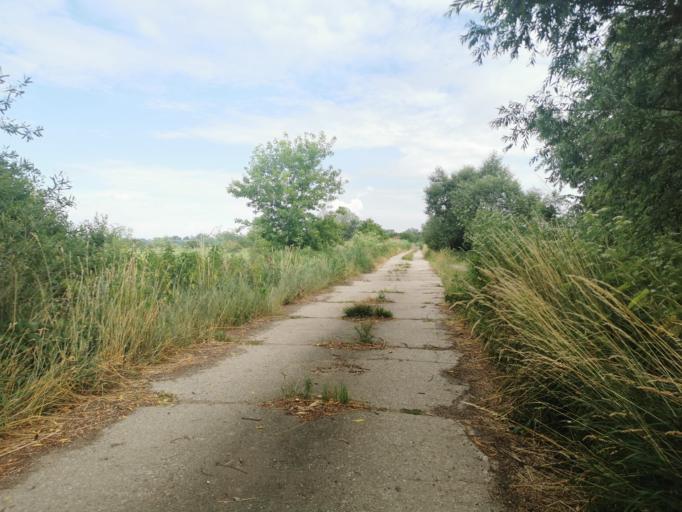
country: CZ
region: South Moravian
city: Tynec
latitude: 48.7650
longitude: 17.0575
